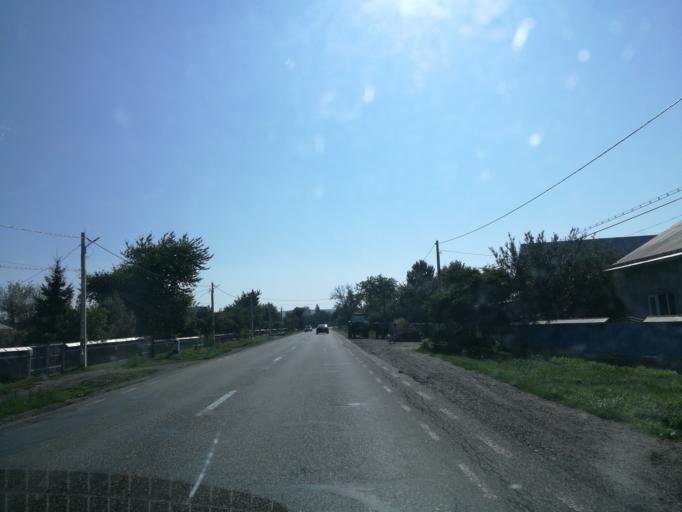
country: RO
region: Suceava
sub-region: Comuna Vadu Moldovei
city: Vadu Moldovei
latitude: 47.3822
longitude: 26.3600
